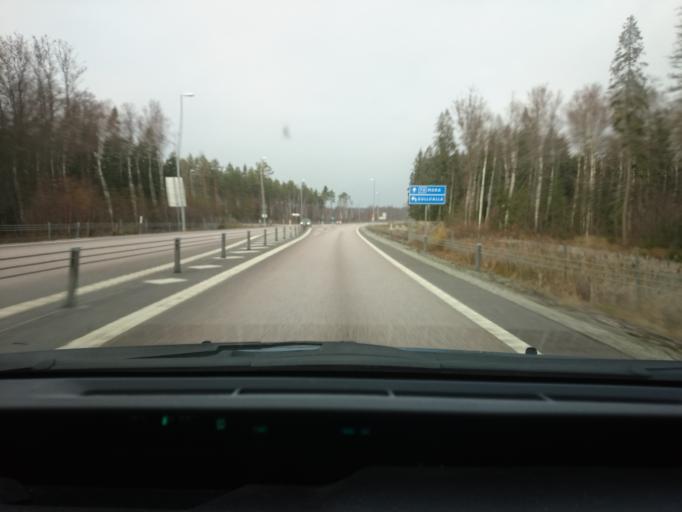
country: SE
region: Vaestmanland
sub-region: Sala Kommun
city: Sala
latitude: 59.9623
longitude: 16.4688
